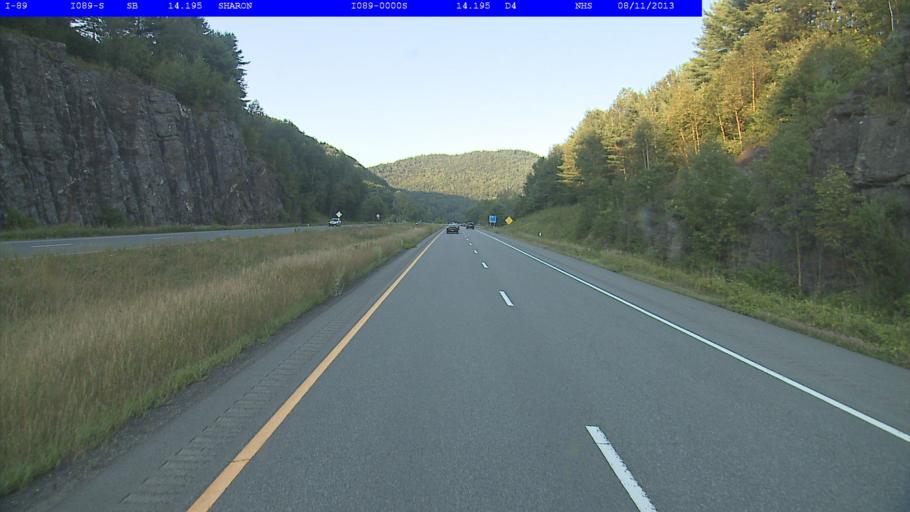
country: US
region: Vermont
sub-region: Windsor County
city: Woodstock
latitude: 43.7832
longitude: -72.4669
